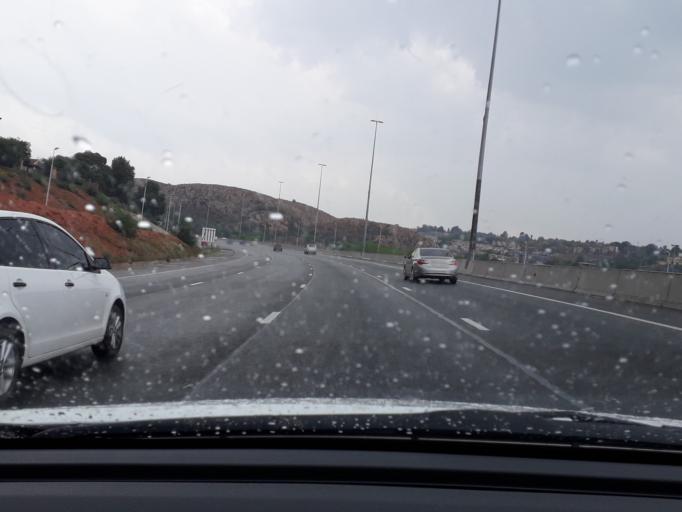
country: ZA
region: Gauteng
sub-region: City of Johannesburg Metropolitan Municipality
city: Roodepoort
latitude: -26.1532
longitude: 27.9272
